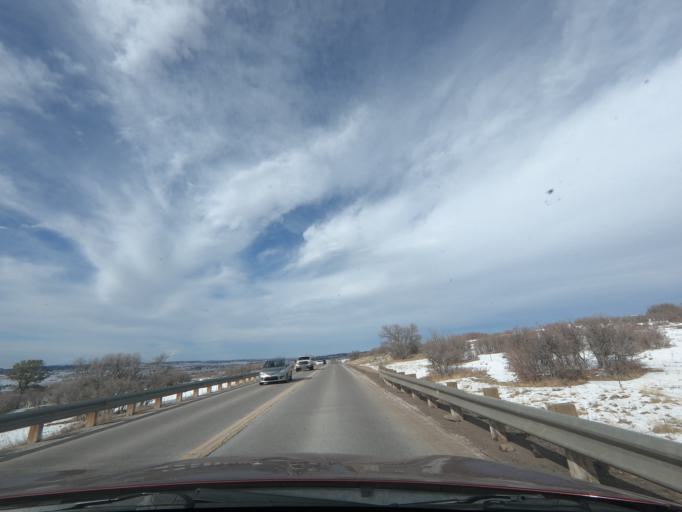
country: US
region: Colorado
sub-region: Douglas County
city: The Pinery
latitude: 39.3647
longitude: -104.7479
